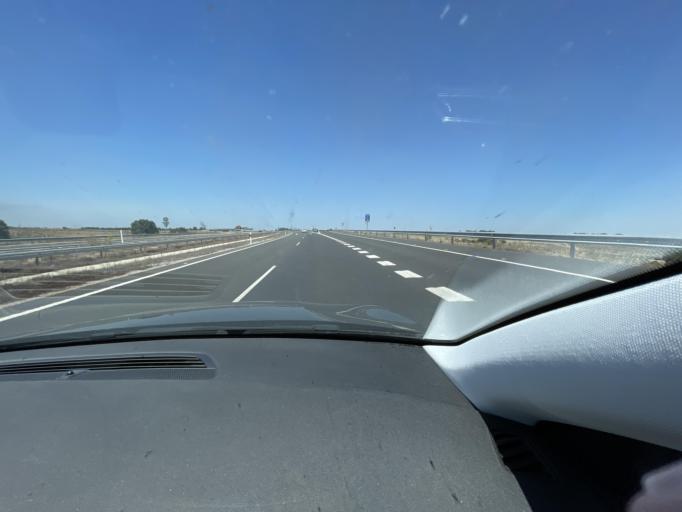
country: ES
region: Castille and Leon
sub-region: Provincia de Salamanca
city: Fuentes de Onoro
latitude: 40.6101
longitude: -6.8155
